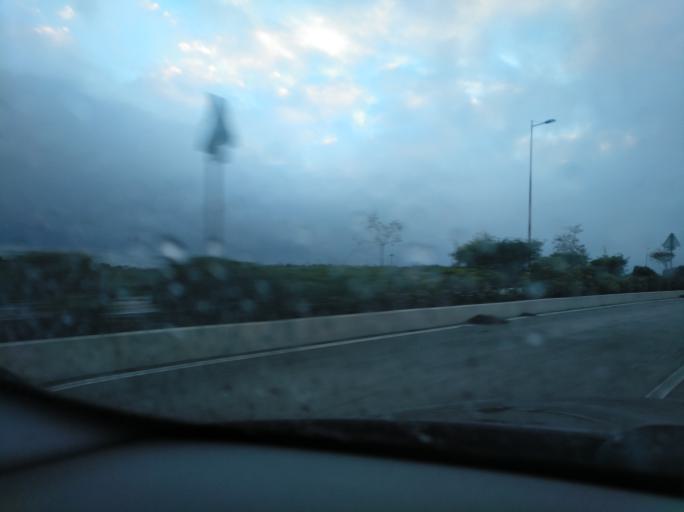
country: PT
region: Faro
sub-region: Castro Marim
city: Castro Marim
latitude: 37.2195
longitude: -7.4522
